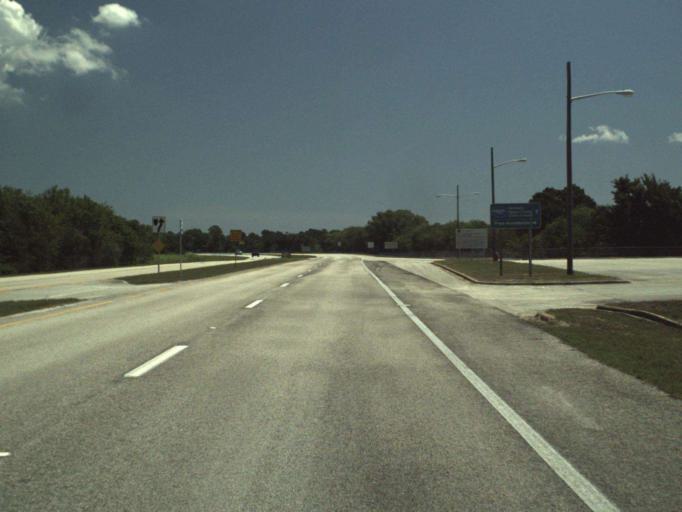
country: US
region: Florida
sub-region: Brevard County
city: Merritt Island
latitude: 28.4809
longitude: -80.6832
